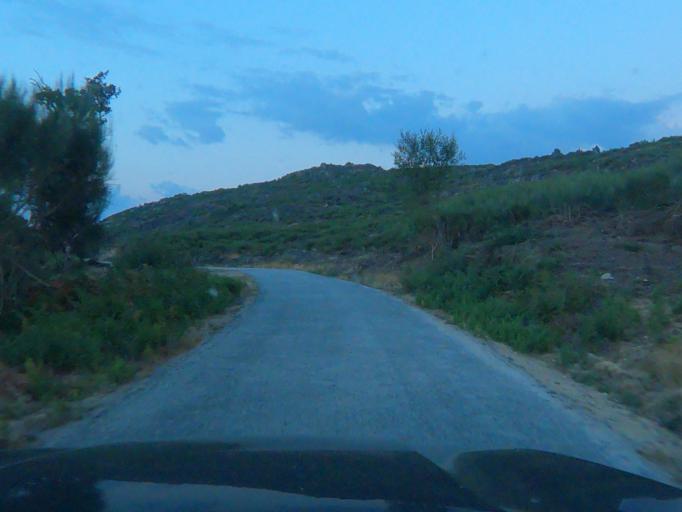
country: PT
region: Vila Real
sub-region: Sabrosa
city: Sabrosa
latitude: 41.2835
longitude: -7.6231
